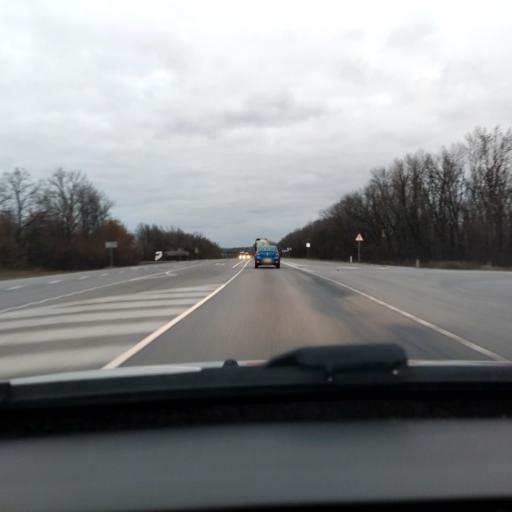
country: RU
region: Lipetsk
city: Borinskoye
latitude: 52.4184
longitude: 39.2532
